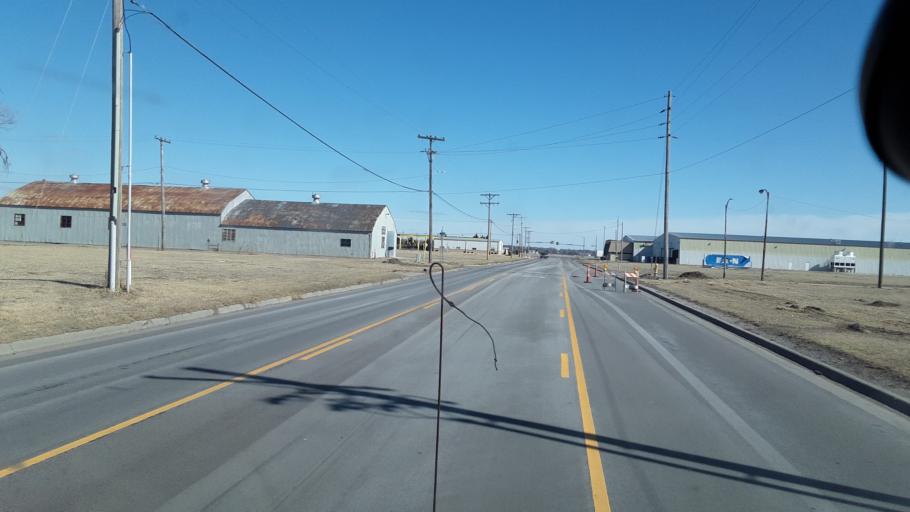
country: US
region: Kansas
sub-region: Reno County
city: Hutchinson
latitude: 38.0576
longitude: -97.8708
